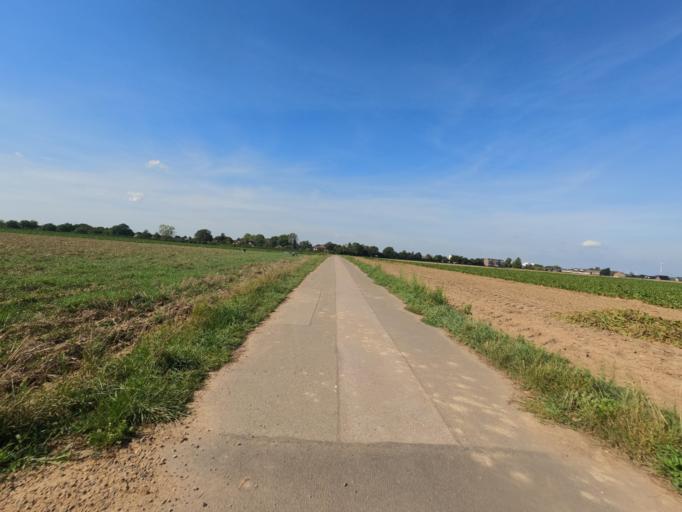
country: DE
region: North Rhine-Westphalia
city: Siersdorf
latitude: 50.9174
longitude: 6.2159
